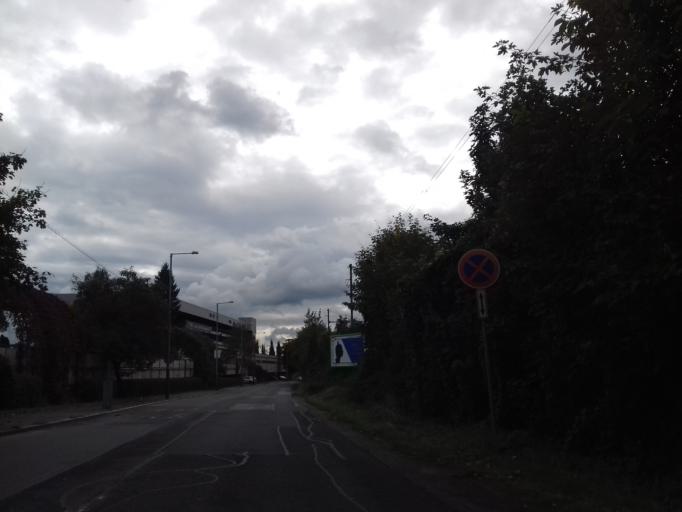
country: CZ
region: Praha
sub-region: Praha 12
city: Modrany
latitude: 50.0106
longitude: 14.3892
